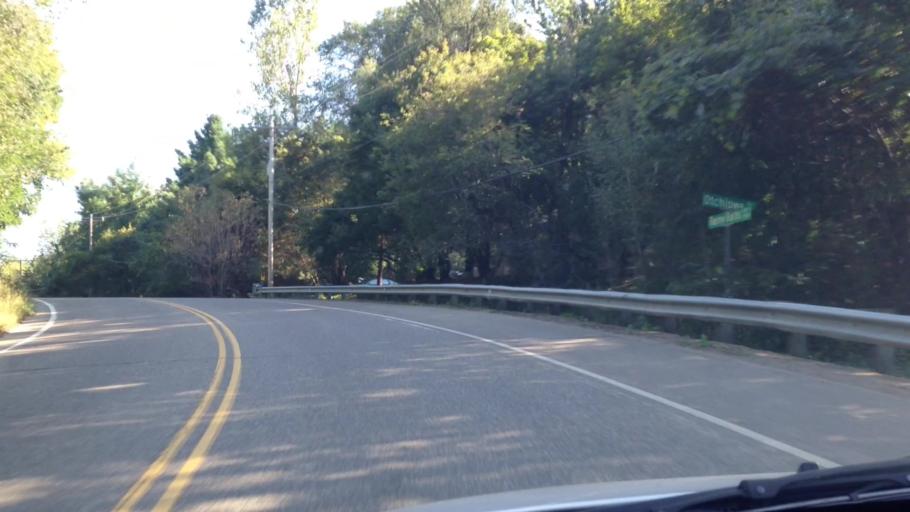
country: US
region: Minnesota
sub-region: Washington County
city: Stillwater
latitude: 45.0827
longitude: -92.8129
